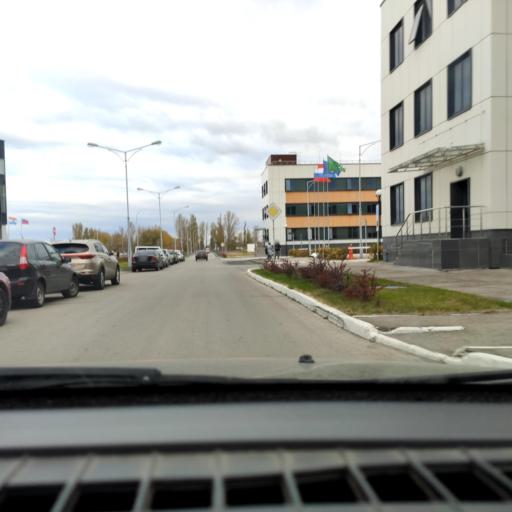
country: RU
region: Samara
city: Podstepki
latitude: 53.5563
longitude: 49.2155
